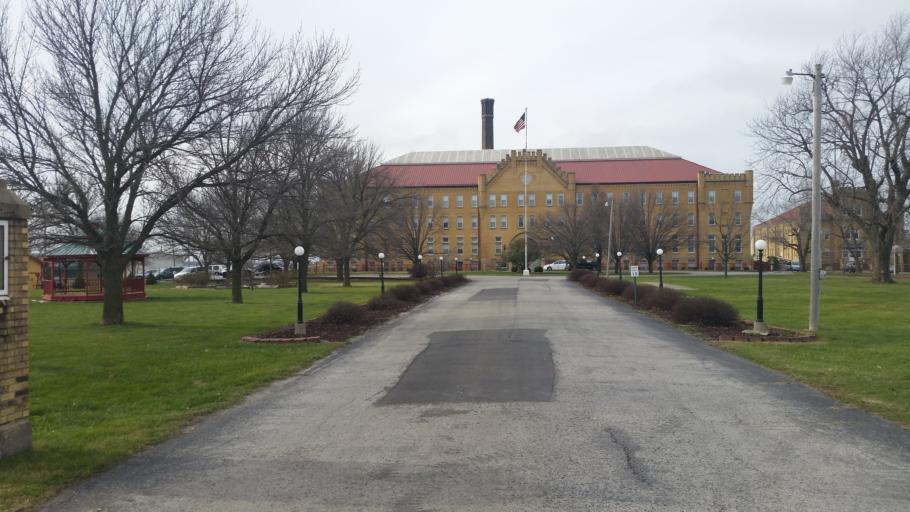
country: US
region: Missouri
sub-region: Macon County
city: Macon
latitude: 39.7204
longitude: -92.4656
